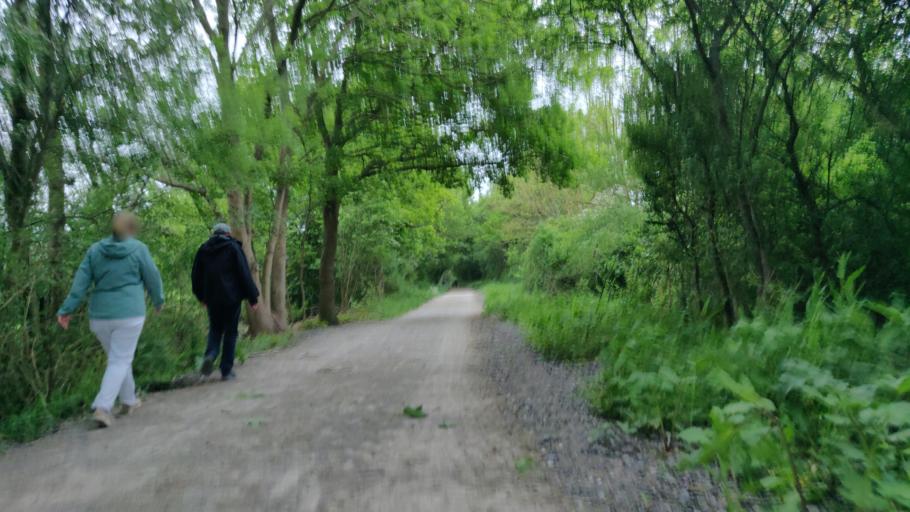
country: GB
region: England
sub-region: West Sussex
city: Partridge Green
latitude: 50.9617
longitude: -0.3122
